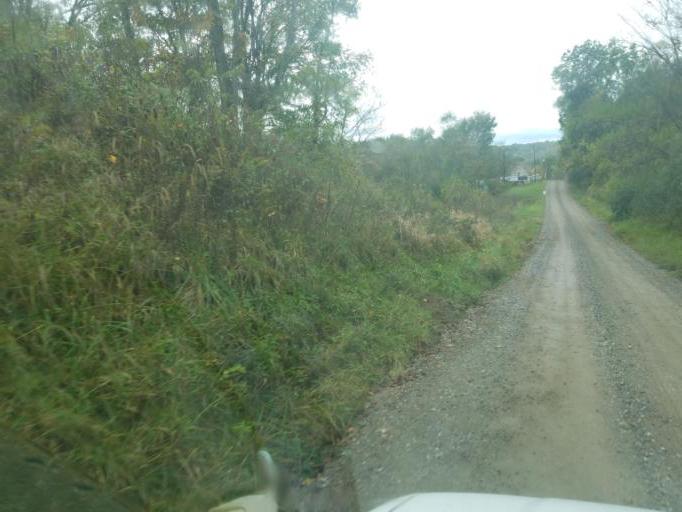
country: US
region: Ohio
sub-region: Holmes County
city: Millersburg
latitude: 40.5356
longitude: -82.0374
